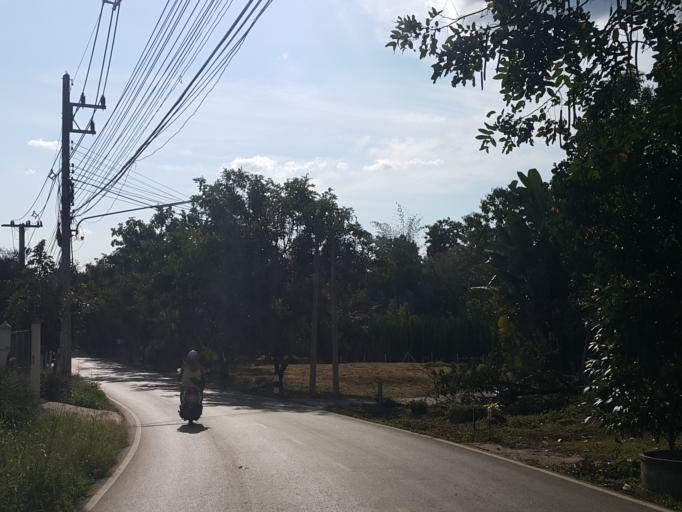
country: TH
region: Chiang Mai
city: Mae On
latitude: 18.8595
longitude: 99.2749
